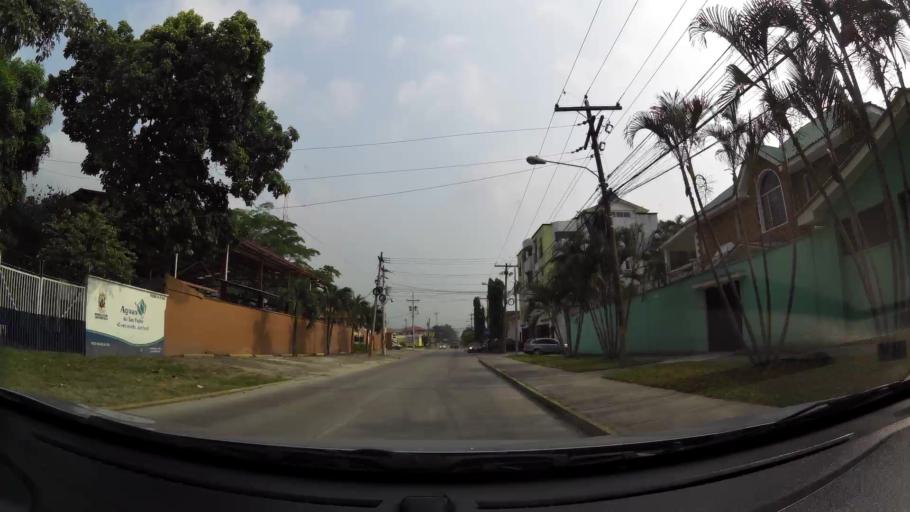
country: HN
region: Cortes
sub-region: San Pedro Sula
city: Pena Blanca
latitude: 15.5340
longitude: -88.0328
